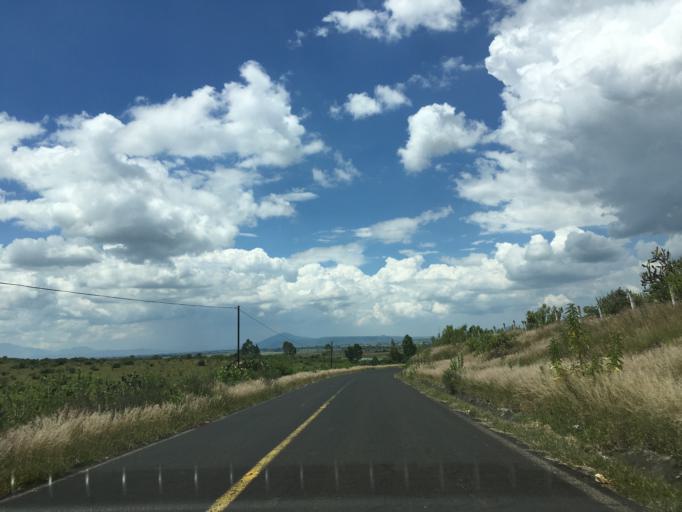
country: MX
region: Mexico
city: Huaniqueo de Morales
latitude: 19.8499
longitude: -101.5338
